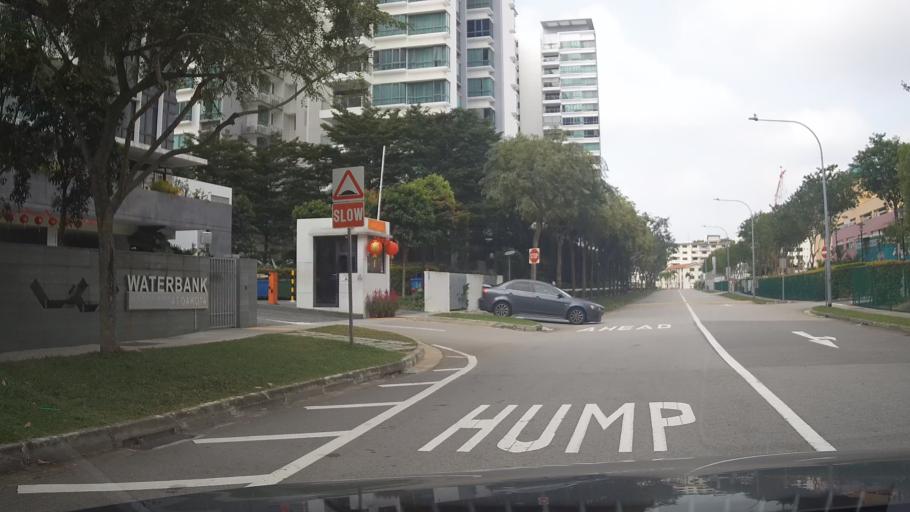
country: SG
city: Singapore
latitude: 1.3070
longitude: 103.8882
